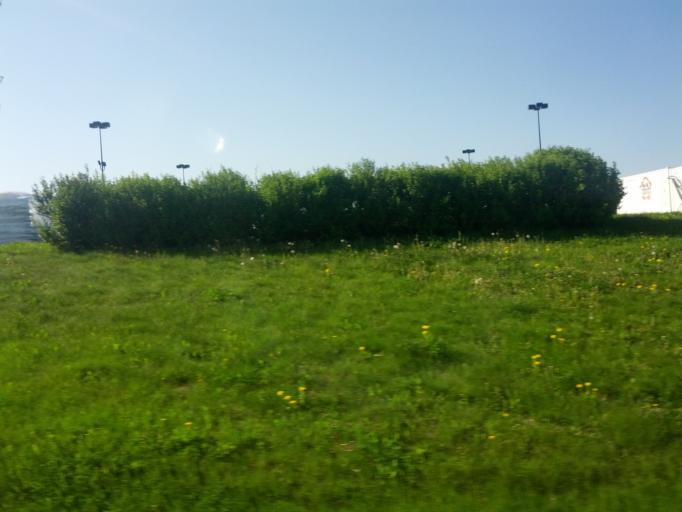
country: CA
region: New Brunswick
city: Moncton
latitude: 46.1137
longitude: -64.8277
